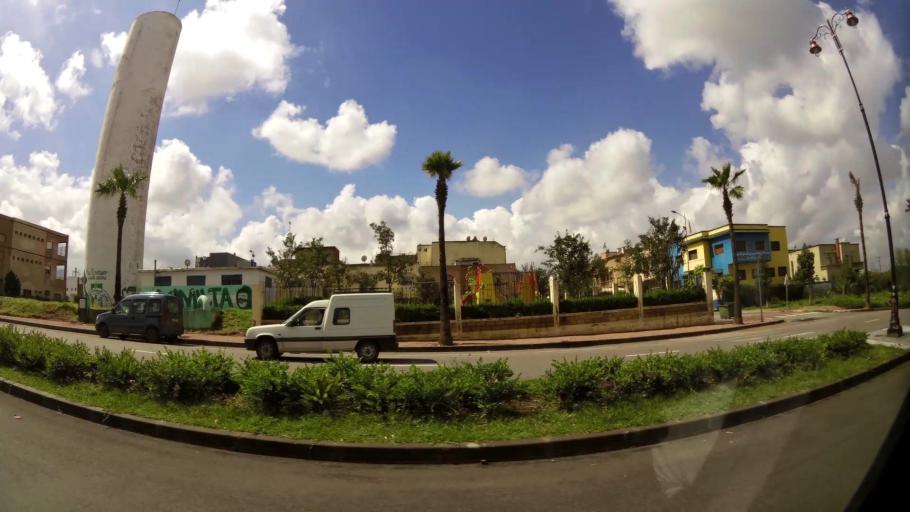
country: MA
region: Grand Casablanca
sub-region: Mediouna
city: Tit Mellil
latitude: 33.5509
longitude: -7.4880
